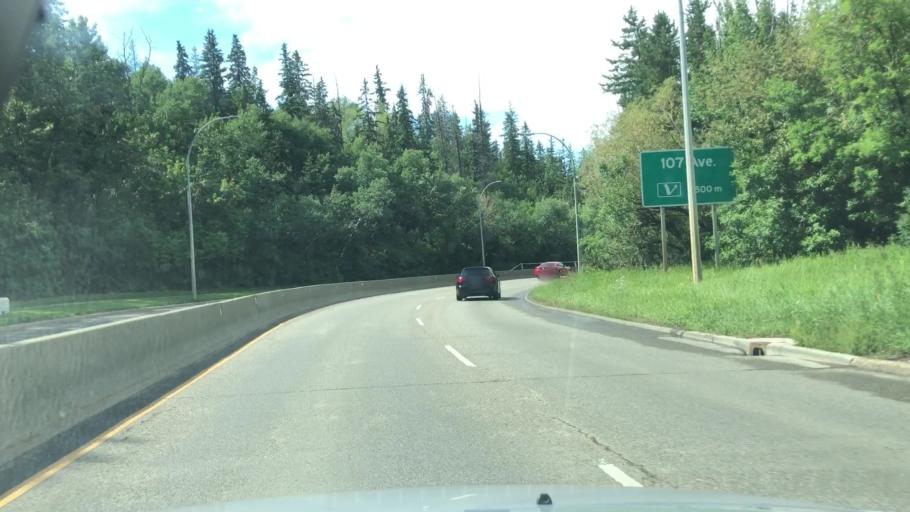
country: CA
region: Alberta
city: Edmonton
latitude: 53.5446
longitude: -113.5416
